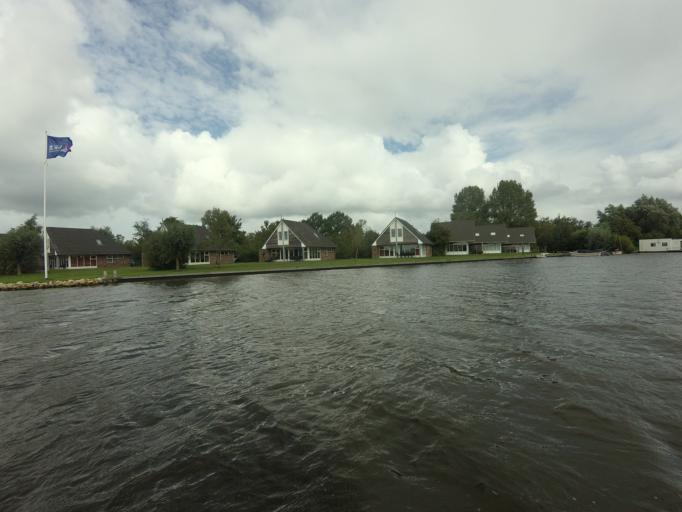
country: NL
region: Friesland
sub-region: Gemeente Boarnsterhim
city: Warten
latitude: 53.1234
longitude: 5.9416
